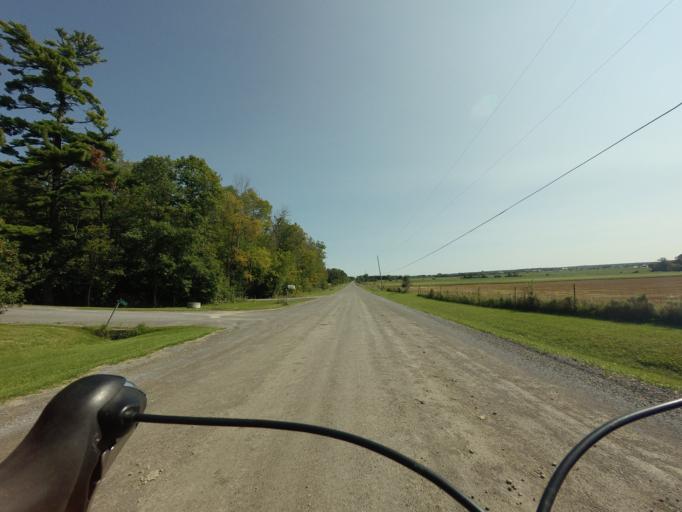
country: CA
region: Ontario
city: Arnprior
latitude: 45.3981
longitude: -76.1736
